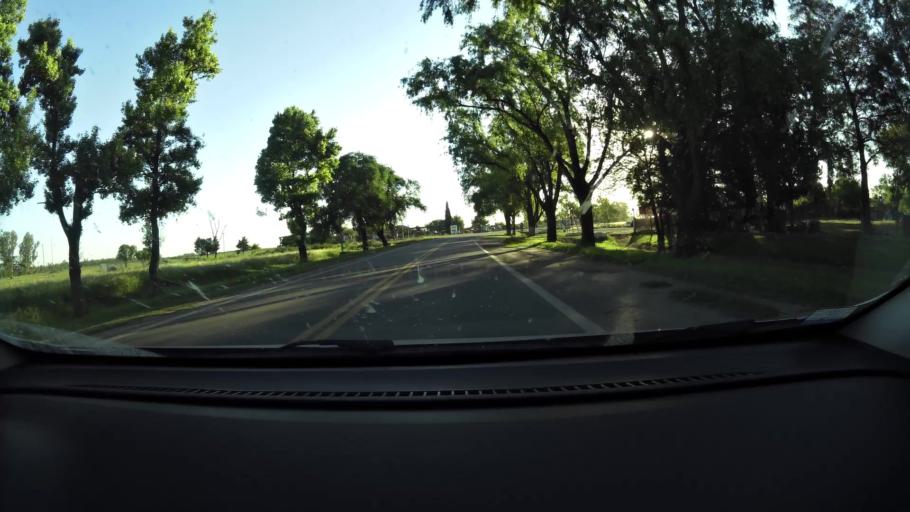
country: AR
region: Cordoba
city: Las Varillas
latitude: -31.8830
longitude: -62.7271
